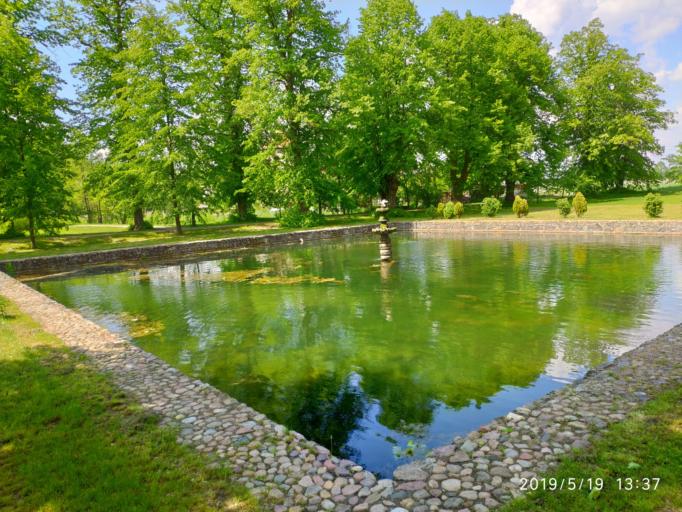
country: PL
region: Lubusz
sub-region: Powiat zielonogorski
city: Czerwiensk
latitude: 52.0378
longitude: 15.3040
